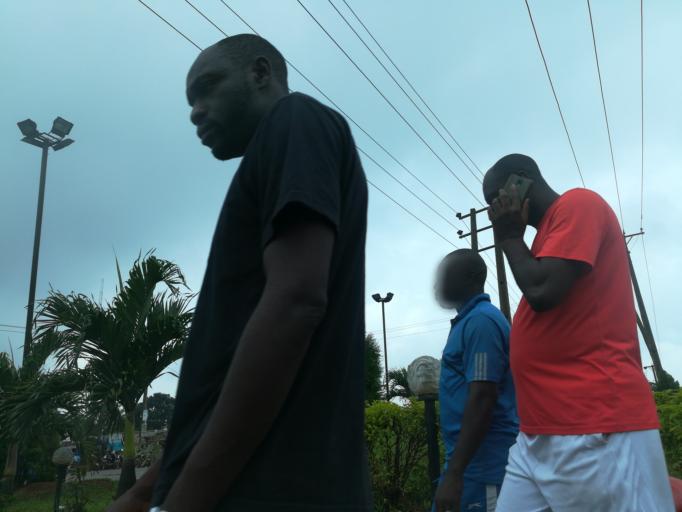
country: NG
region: Lagos
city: Ikorodu
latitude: 6.6463
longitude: 3.5176
